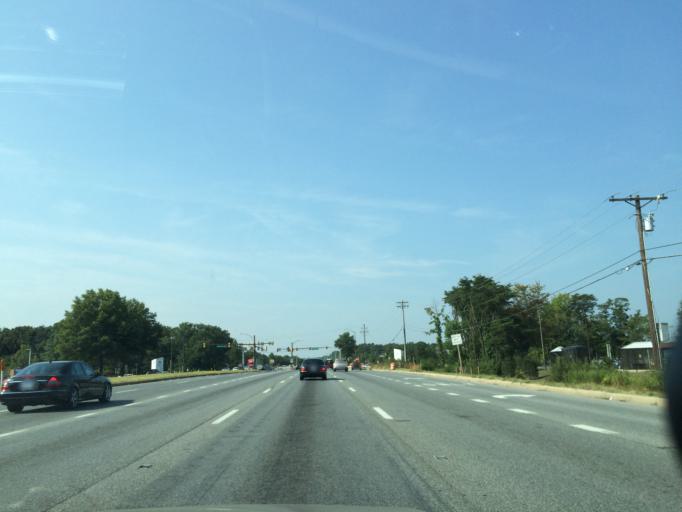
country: US
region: Maryland
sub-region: Charles County
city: Saint Charles
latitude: 38.6129
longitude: -76.9245
